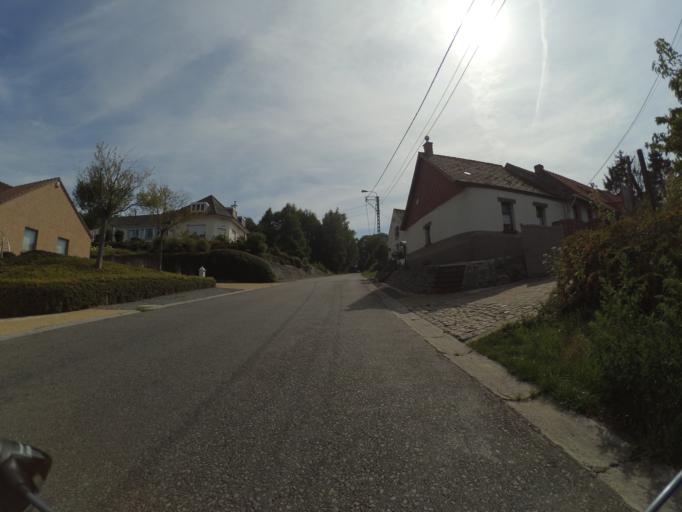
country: BE
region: Wallonia
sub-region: Province du Hainaut
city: Frasnes-lez-Anvaing
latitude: 50.7141
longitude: 3.6223
